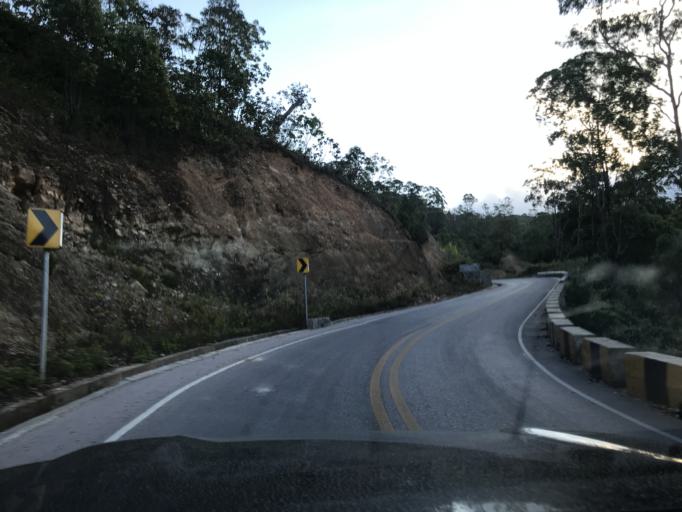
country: TL
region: Aileu
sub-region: Aileu Villa
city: Aileu
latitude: -8.6922
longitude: 125.5501
